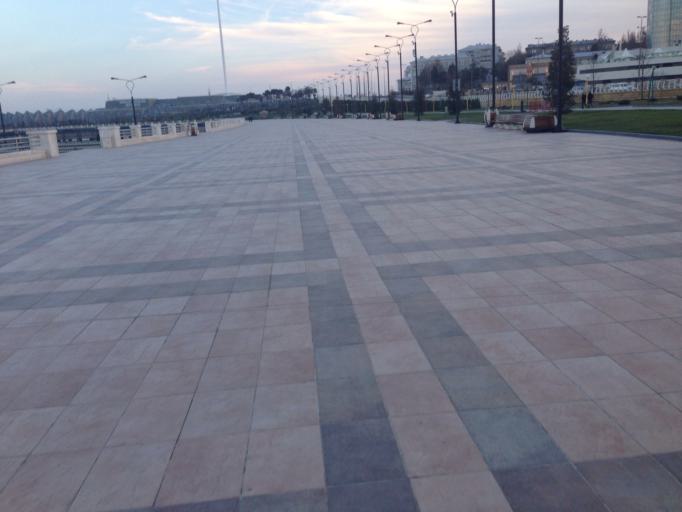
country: AZ
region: Baki
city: Badamdar
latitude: 40.3490
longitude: 49.8381
